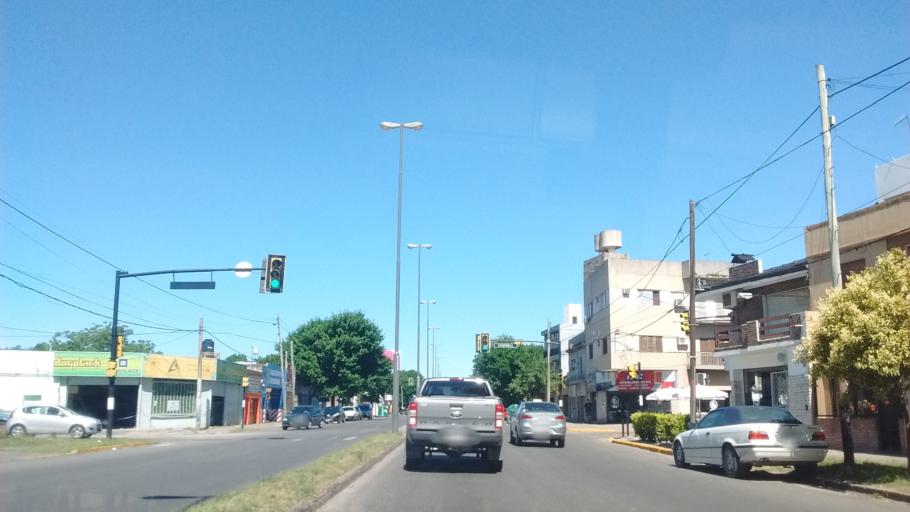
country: AR
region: Santa Fe
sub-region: Departamento de Rosario
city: Rosario
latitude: -32.9338
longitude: -60.7087
